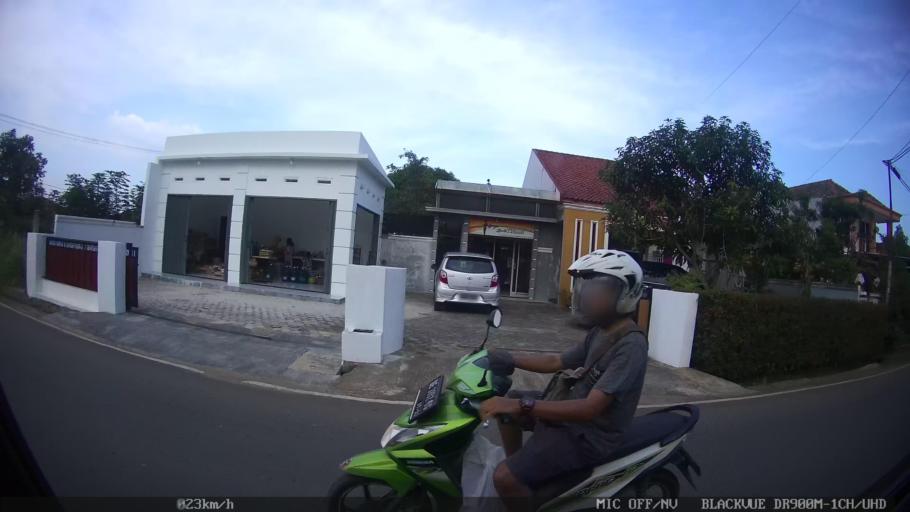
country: ID
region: Lampung
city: Kedaton
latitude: -5.3861
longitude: 105.2332
